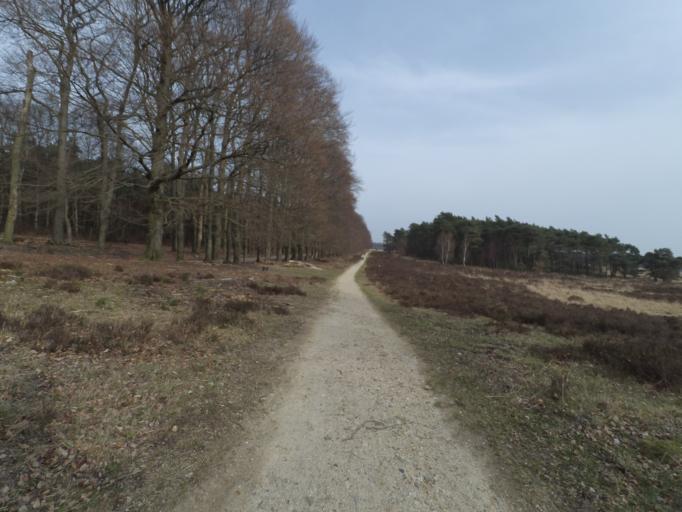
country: NL
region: Gelderland
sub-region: Gemeente Renkum
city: Wolfheze
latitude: 52.0426
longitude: 5.7865
